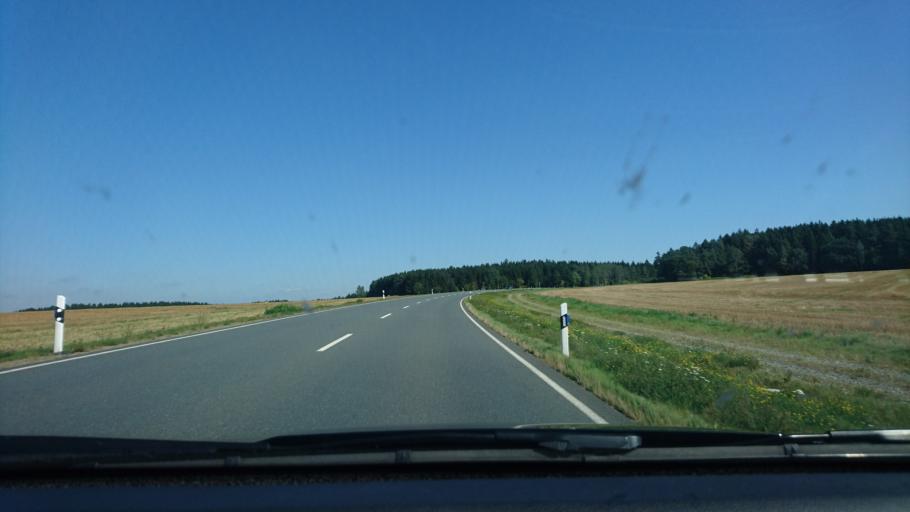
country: DE
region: Saxony
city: Lengenfeld
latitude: 50.5424
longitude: 12.3554
